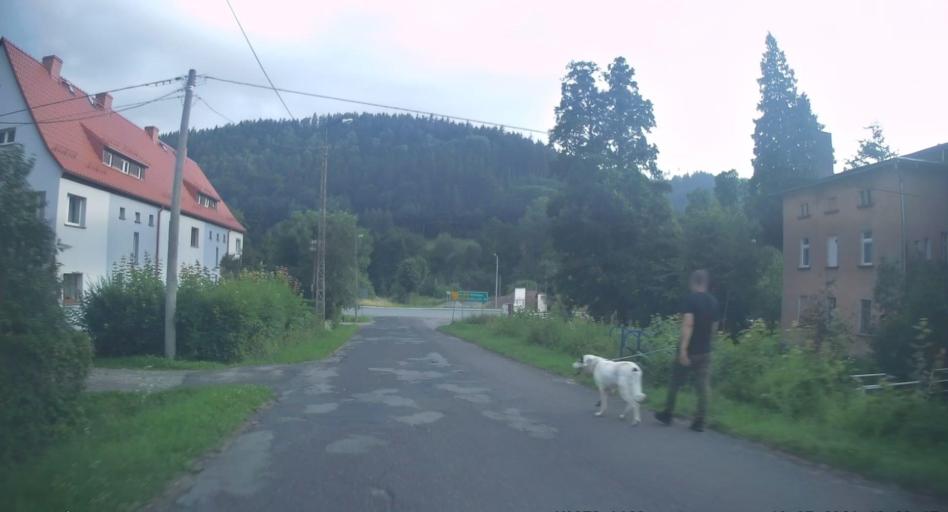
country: PL
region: Lower Silesian Voivodeship
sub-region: Powiat klodzki
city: Ludwikowice Klodzkie
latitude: 50.6244
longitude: 16.4616
